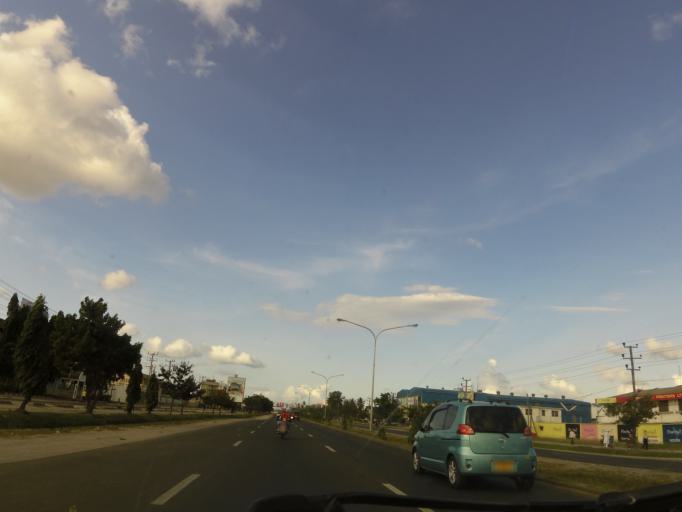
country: TZ
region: Dar es Salaam
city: Dar es Salaam
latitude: -6.8543
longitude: 39.2249
